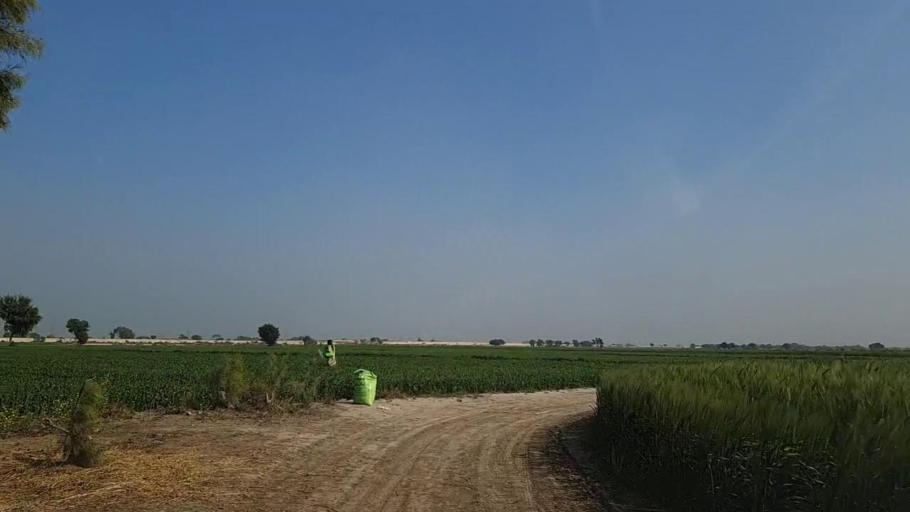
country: PK
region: Sindh
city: Moro
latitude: 26.6797
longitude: 67.9372
